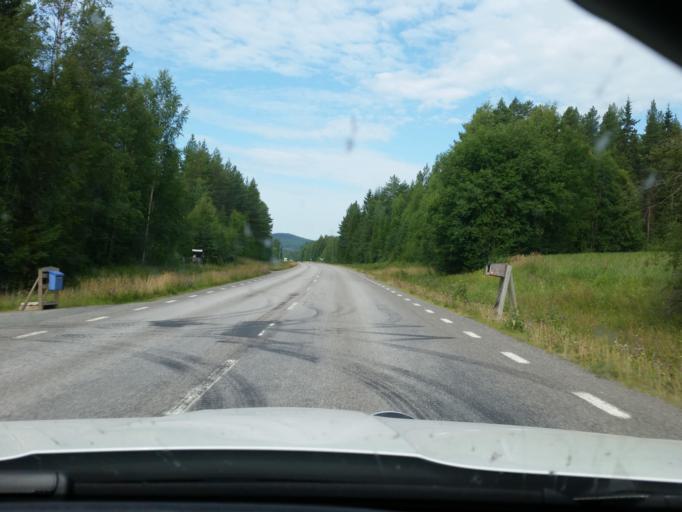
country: SE
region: Norrbotten
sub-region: Alvsbyns Kommun
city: AElvsbyn
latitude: 65.6780
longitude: 20.8233
